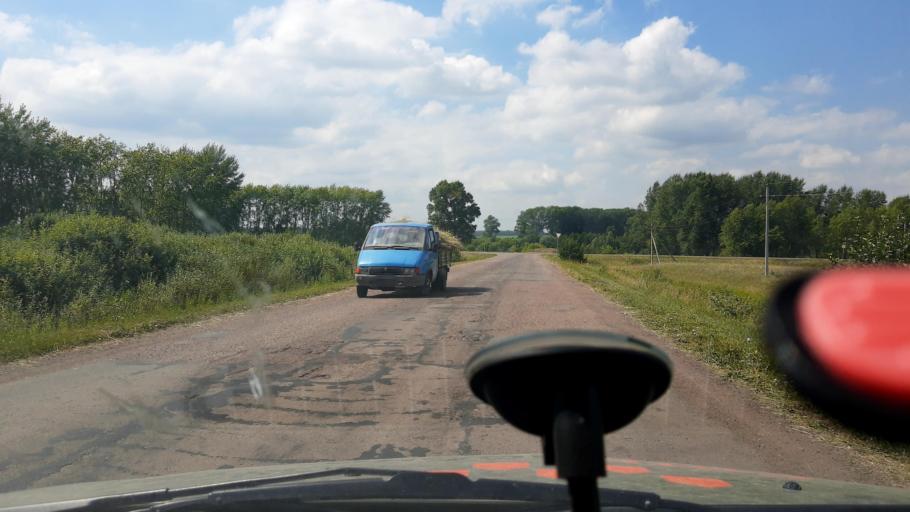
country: RU
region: Bashkortostan
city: Chekmagush
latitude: 54.8886
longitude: 54.5803
